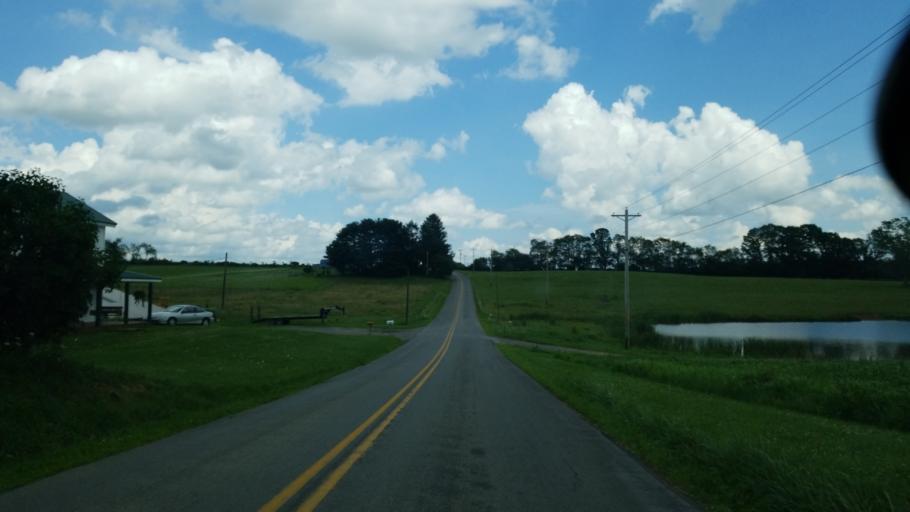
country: US
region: Pennsylvania
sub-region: Jefferson County
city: Brookville
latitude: 41.2391
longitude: -79.0327
